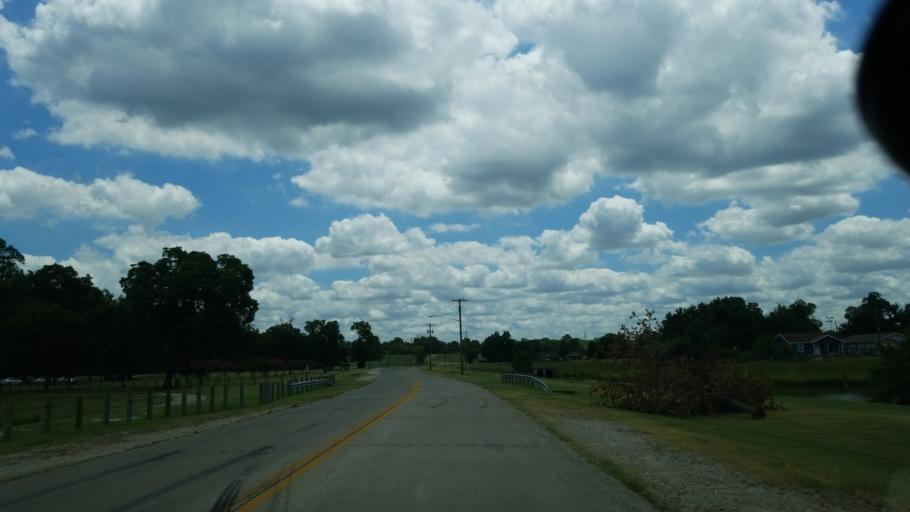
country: US
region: Texas
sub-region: Dallas County
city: Dallas
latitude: 32.7439
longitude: -96.7456
